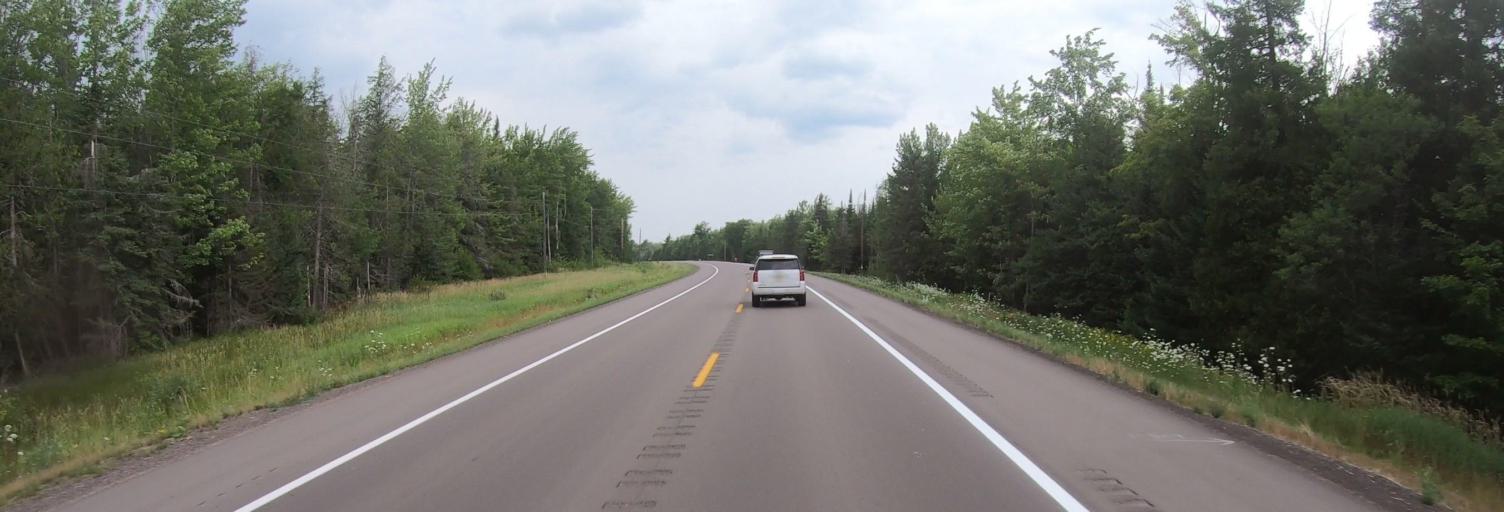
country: US
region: Michigan
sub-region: Baraga County
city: Baraga
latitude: 46.9484
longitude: -88.4504
